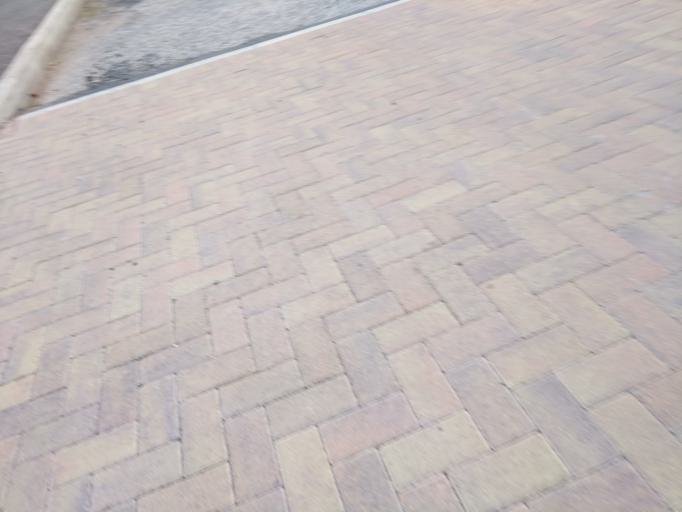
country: GB
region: Scotland
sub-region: Edinburgh
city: Colinton
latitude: 55.9319
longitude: -3.2437
